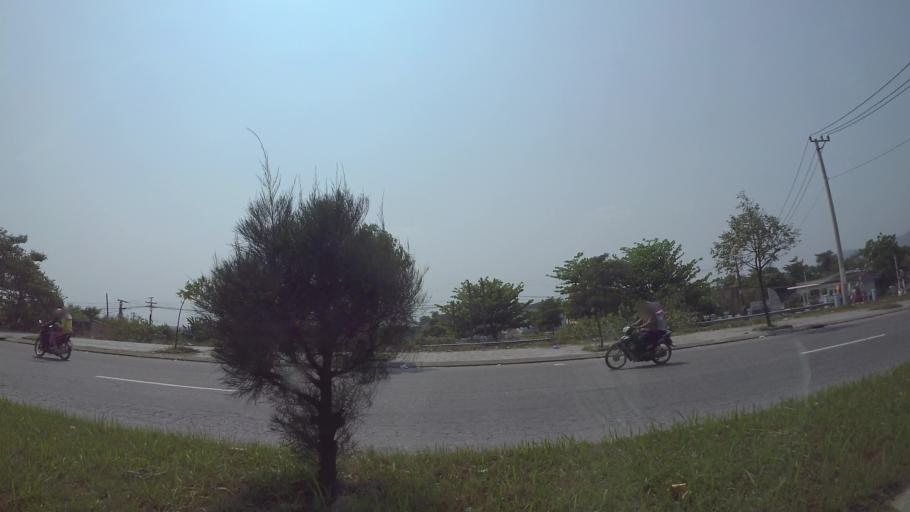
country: VN
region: Da Nang
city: Cam Le
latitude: 16.0013
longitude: 108.1905
